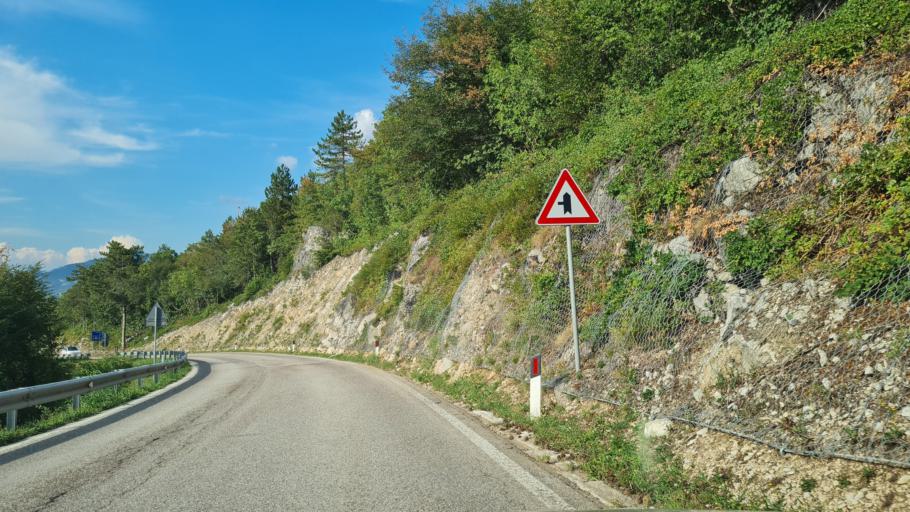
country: IT
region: Trentino-Alto Adige
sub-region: Provincia di Trento
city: Mattarello
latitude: 46.0199
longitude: 11.1453
